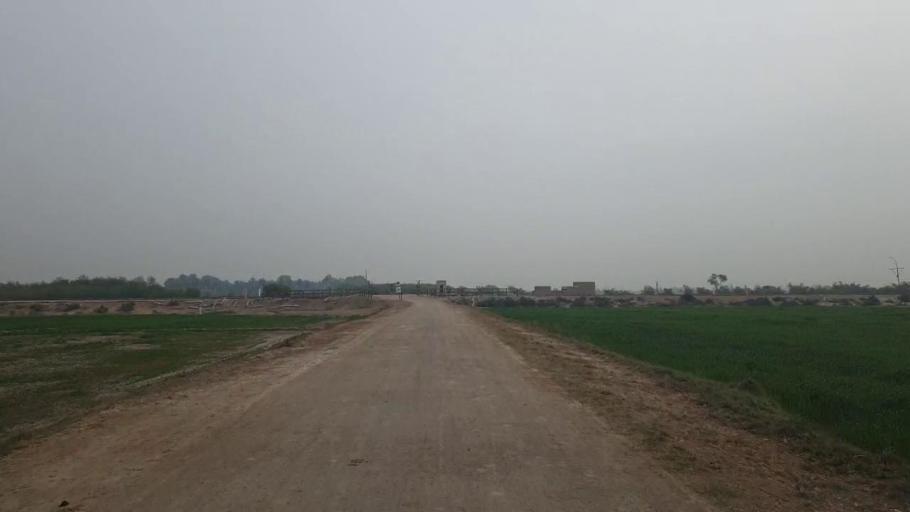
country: PK
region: Sindh
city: Tando Adam
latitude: 25.8127
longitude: 68.6623
